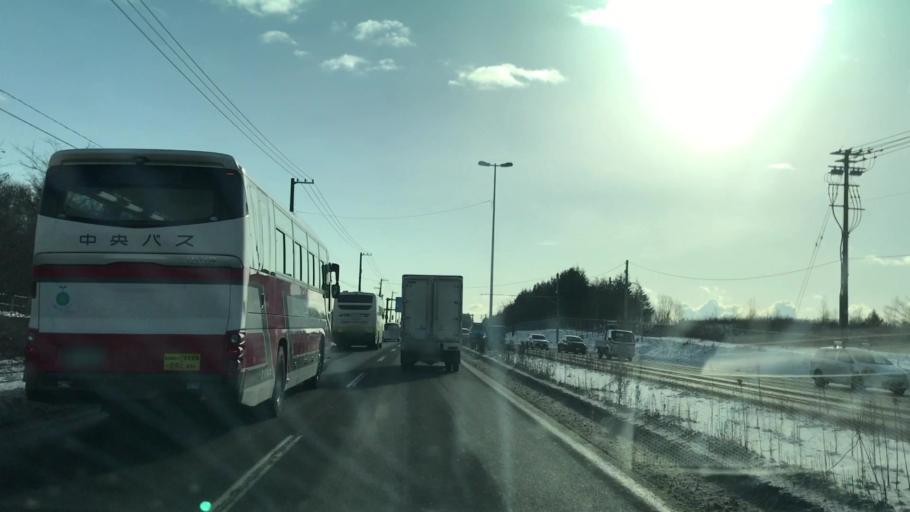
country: JP
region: Hokkaido
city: Chitose
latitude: 42.8185
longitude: 141.6626
